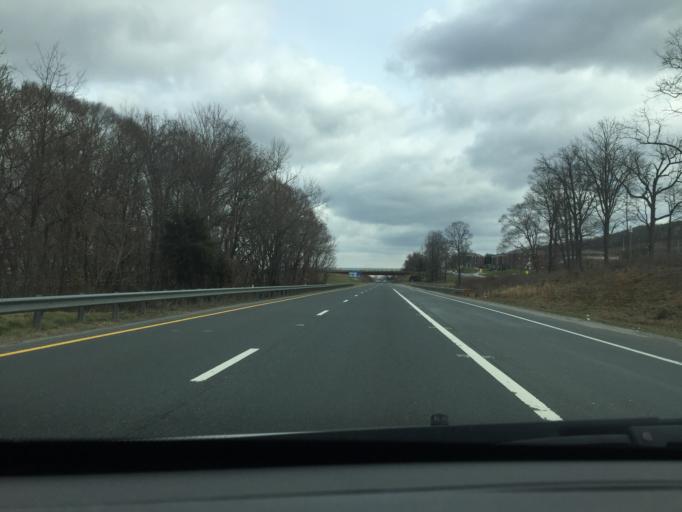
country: US
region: Virginia
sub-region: City of Lynchburg
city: West Lynchburg
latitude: 37.3495
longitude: -79.1773
